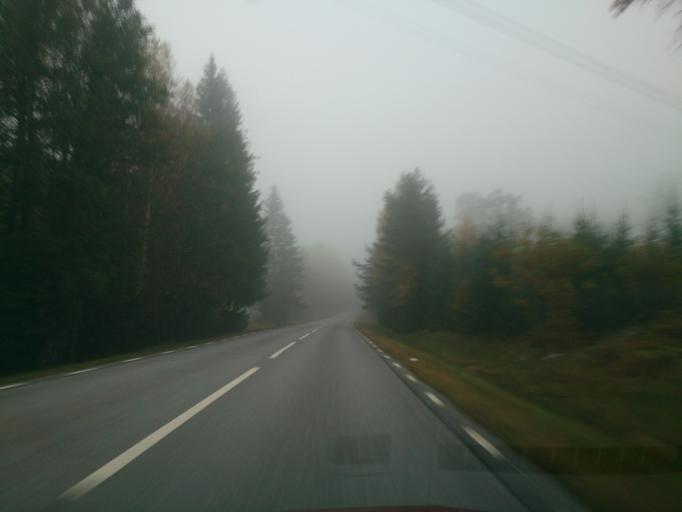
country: SE
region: OEstergoetland
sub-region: Atvidabergs Kommun
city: Atvidaberg
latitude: 58.1459
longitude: 15.9613
